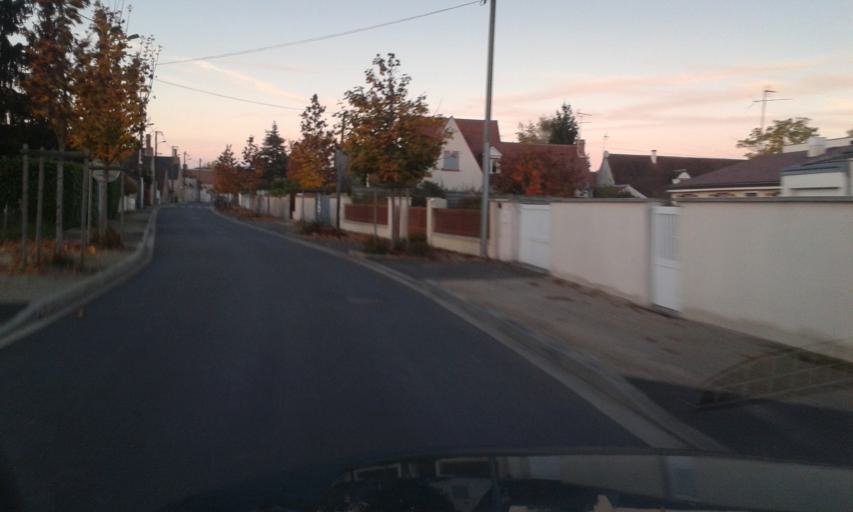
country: FR
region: Centre
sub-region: Departement du Loiret
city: Olivet
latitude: 47.8513
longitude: 1.8829
